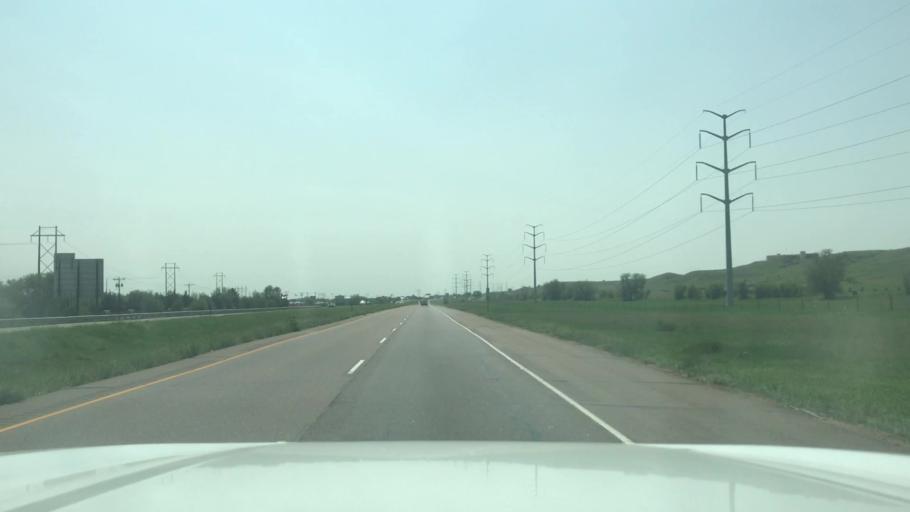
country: US
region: Colorado
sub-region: El Paso County
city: Security-Widefield
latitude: 38.7164
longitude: -104.7276
